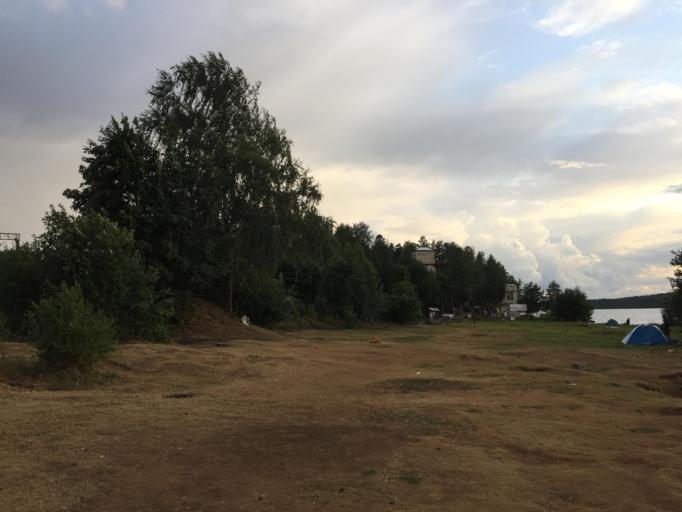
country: RU
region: Leningrad
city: Toksovo
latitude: 60.1743
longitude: 30.5263
